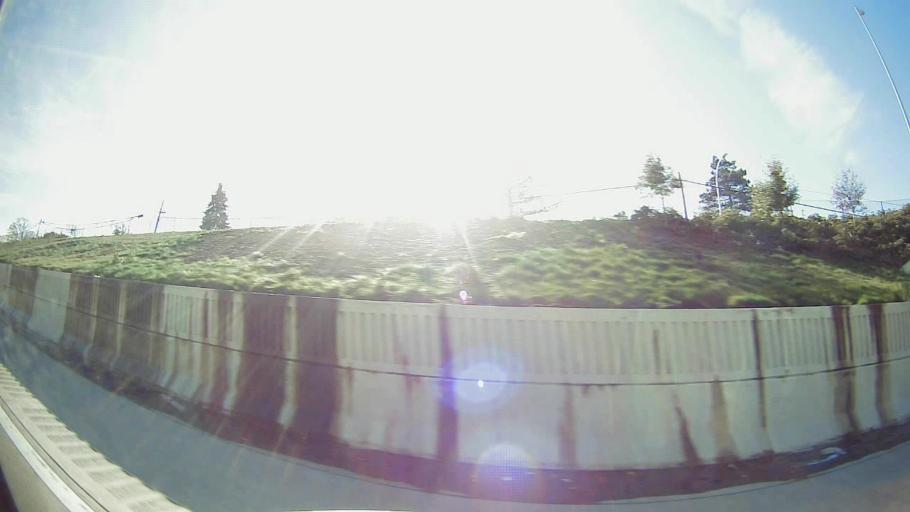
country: US
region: Michigan
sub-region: Wayne County
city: Livonia
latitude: 42.3821
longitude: -83.3881
